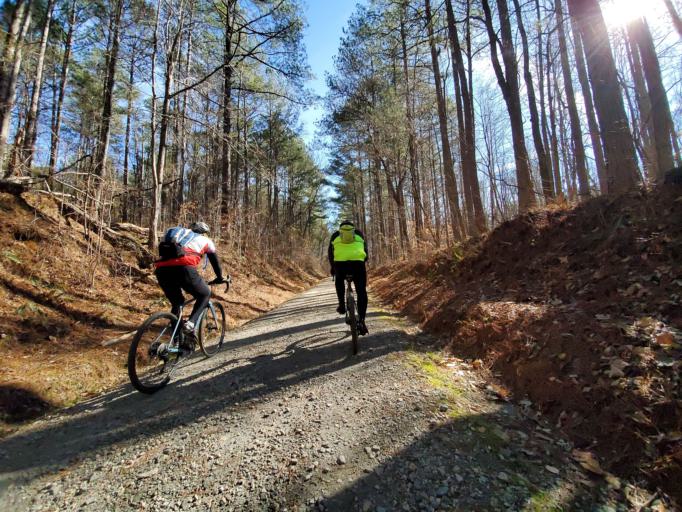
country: US
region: Georgia
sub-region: Fulton County
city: Chattahoochee Hills
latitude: 33.5711
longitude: -84.7153
